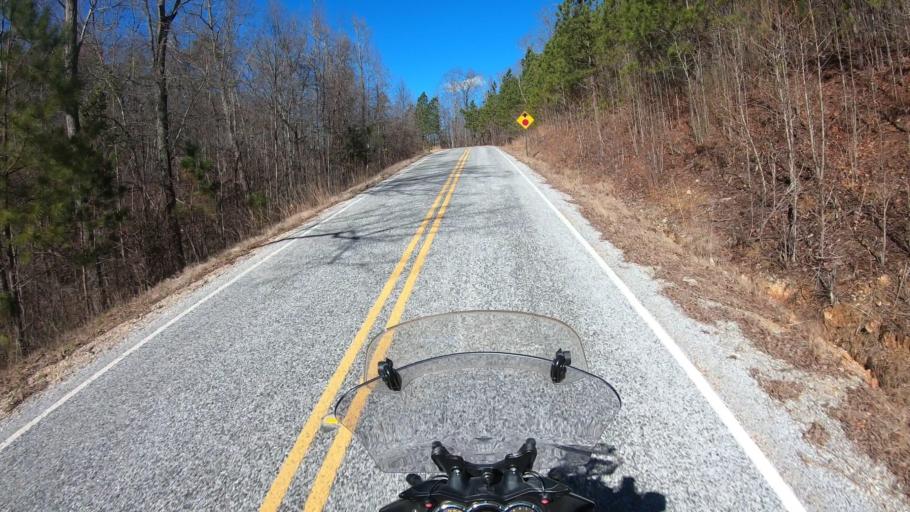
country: US
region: Alabama
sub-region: Clay County
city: Ashland
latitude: 33.4036
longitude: -85.8736
